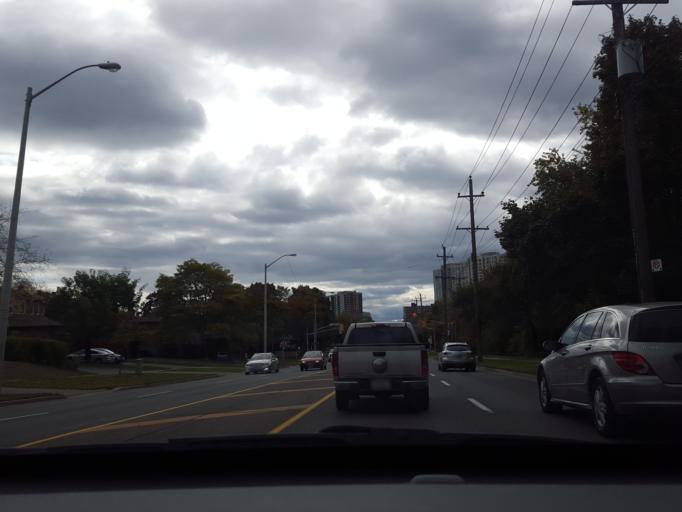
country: CA
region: Ontario
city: Scarborough
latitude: 43.7921
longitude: -79.2922
